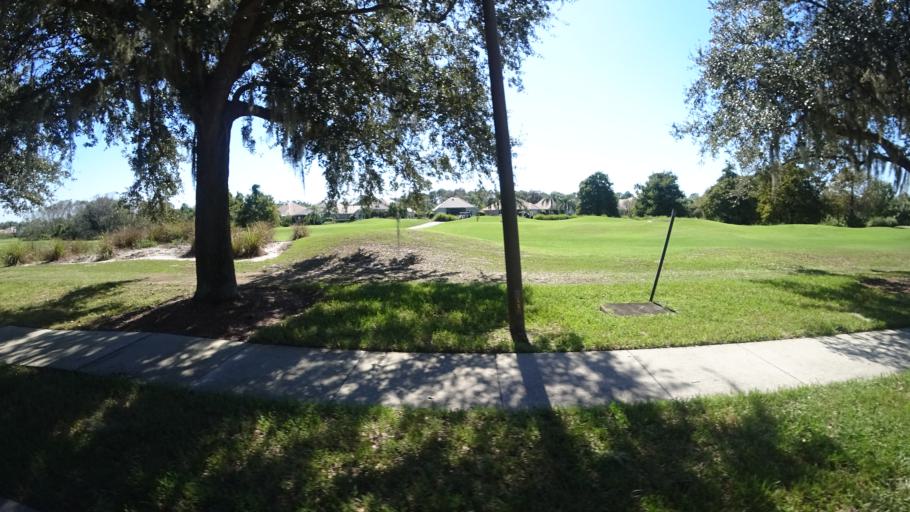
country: US
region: Florida
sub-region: Sarasota County
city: The Meadows
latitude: 27.4020
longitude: -82.4280
